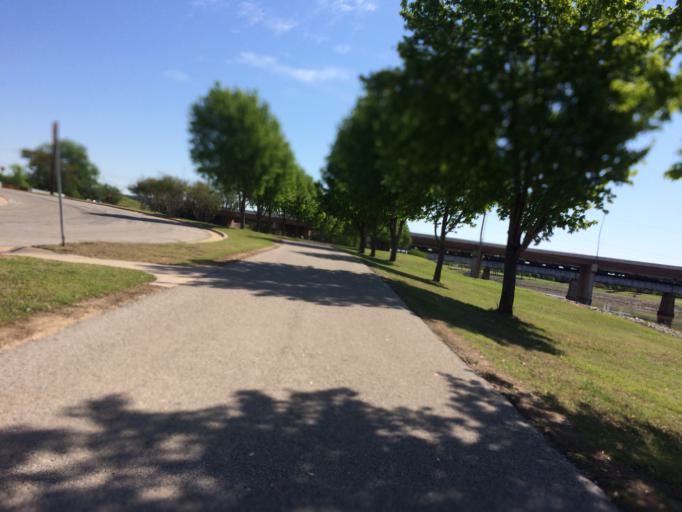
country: US
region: Oklahoma
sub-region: Oklahoma County
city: Oklahoma City
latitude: 35.4490
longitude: -97.5157
